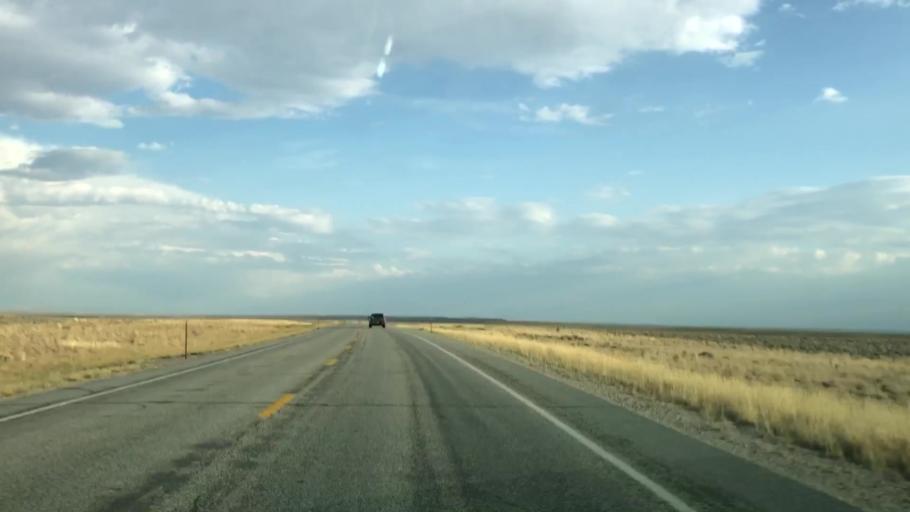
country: US
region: Wyoming
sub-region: Sublette County
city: Marbleton
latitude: 42.3363
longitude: -109.5199
